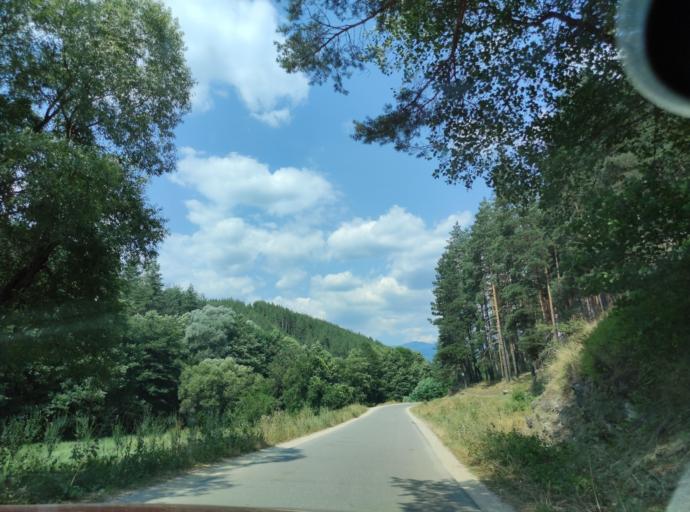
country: BG
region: Blagoevgrad
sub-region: Obshtina Belitsa
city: Belitsa
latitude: 41.9628
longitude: 23.5554
